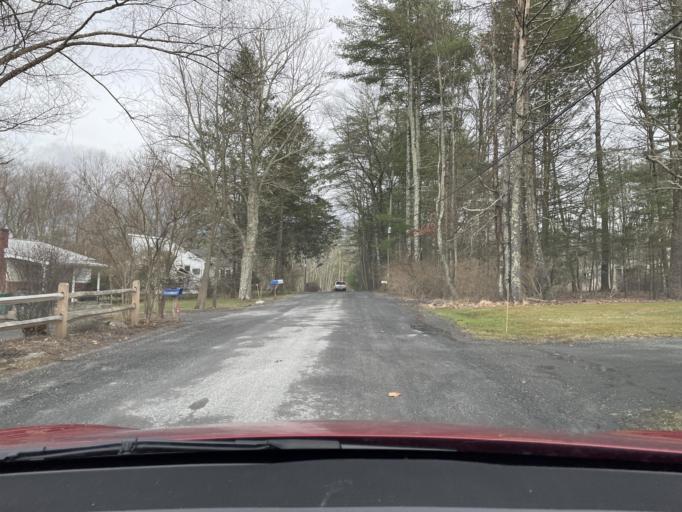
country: US
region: New York
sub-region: Ulster County
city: Woodstock
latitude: 42.0279
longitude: -74.1043
